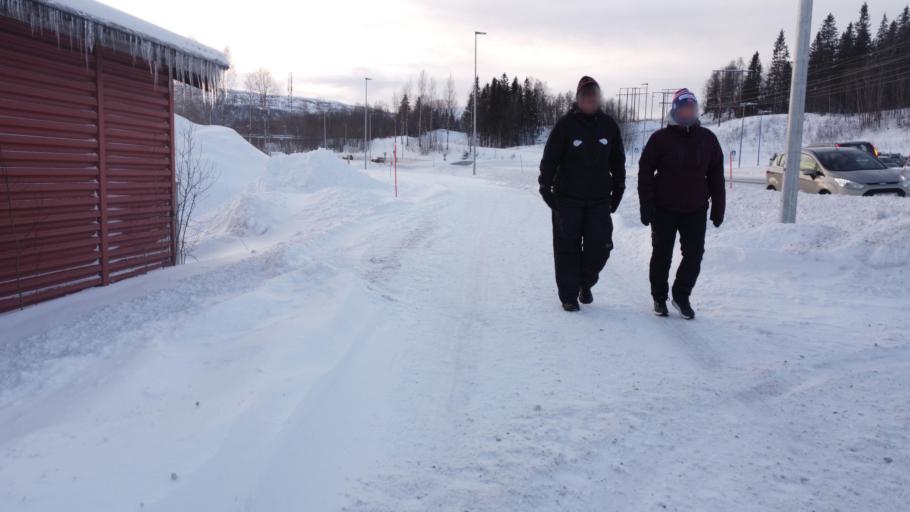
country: NO
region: Nordland
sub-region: Rana
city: Mo i Rana
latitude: 66.3288
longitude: 14.1600
